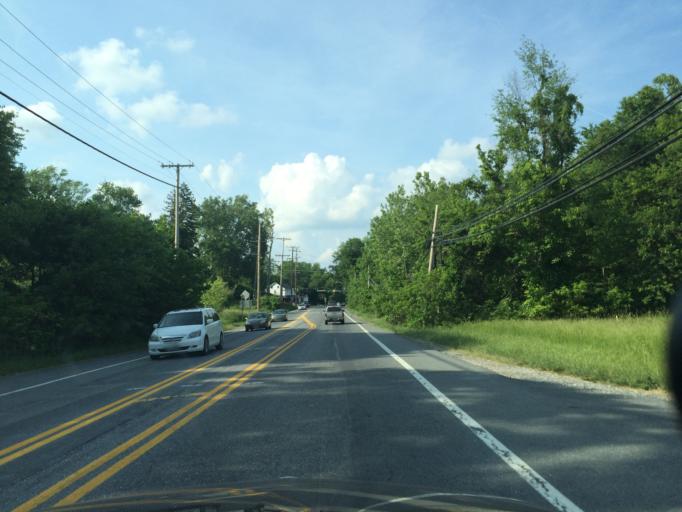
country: US
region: Maryland
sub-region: Carroll County
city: Sykesville
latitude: 39.3188
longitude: -77.0200
